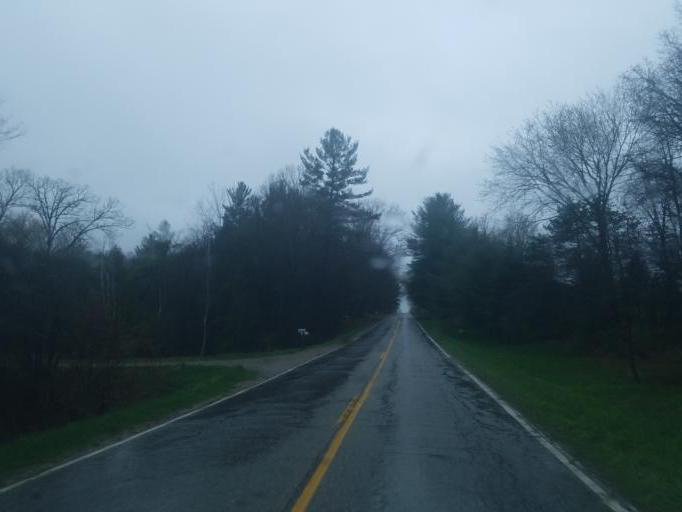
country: US
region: Michigan
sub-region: Montcalm County
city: Edmore
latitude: 43.5197
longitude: -85.0259
